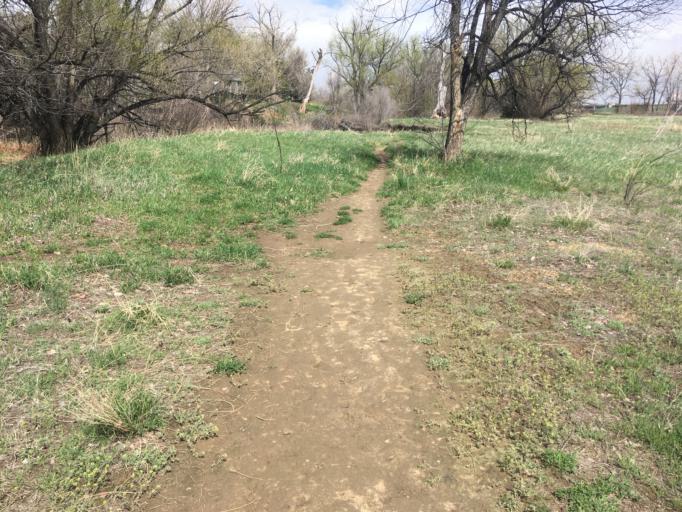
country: US
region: Colorado
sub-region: Boulder County
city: Gunbarrel
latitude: 40.0503
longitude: -105.1865
